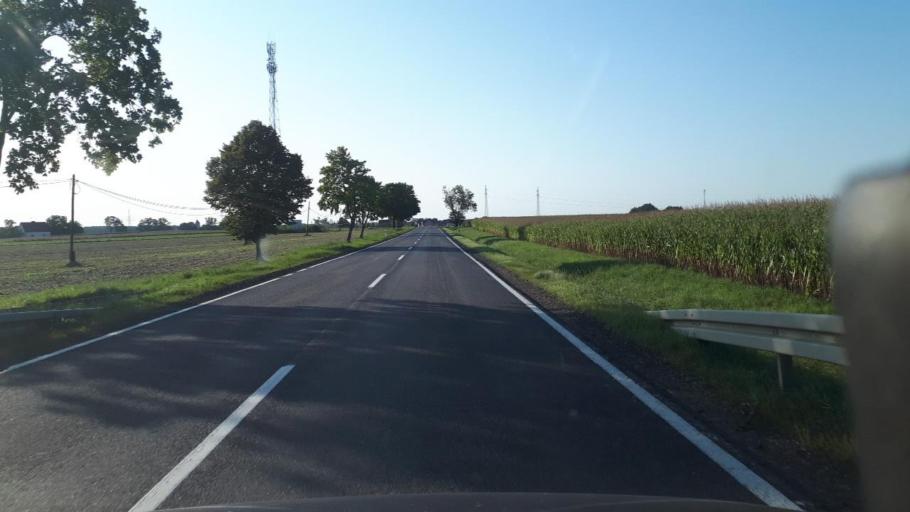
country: PL
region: Silesian Voivodeship
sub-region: Powiat lubliniecki
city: Sierakow Slaski
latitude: 50.8388
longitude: 18.5066
